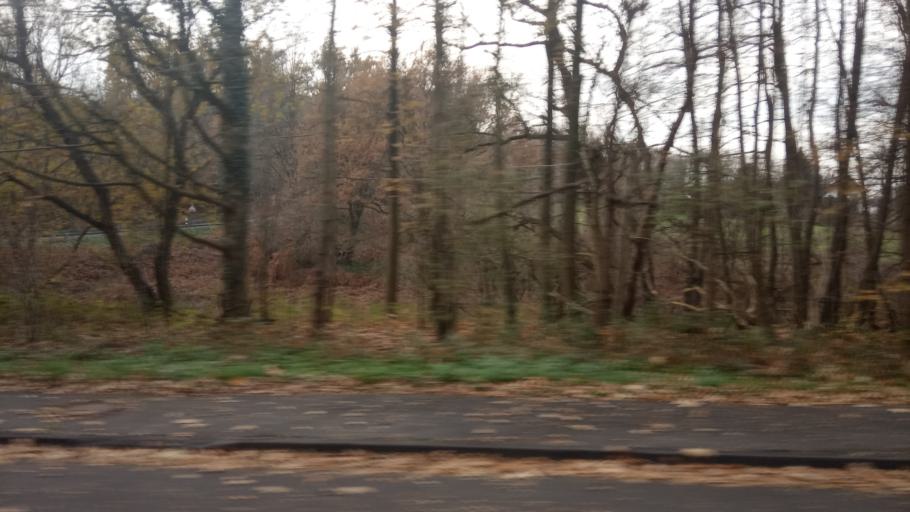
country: DE
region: North Rhine-Westphalia
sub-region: Regierungsbezirk Dusseldorf
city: Velbert
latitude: 51.3802
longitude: 7.0635
